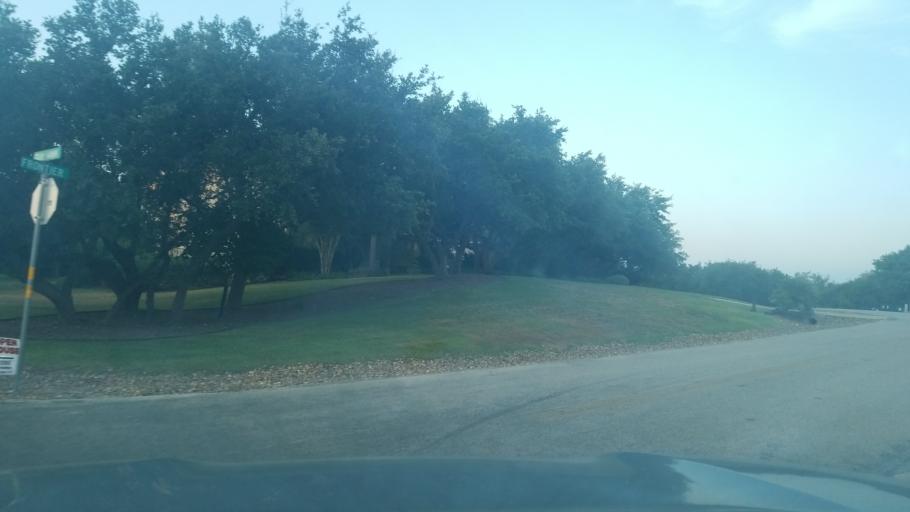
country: US
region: Texas
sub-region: Comal County
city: Bulverde
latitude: 29.8347
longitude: -98.4032
